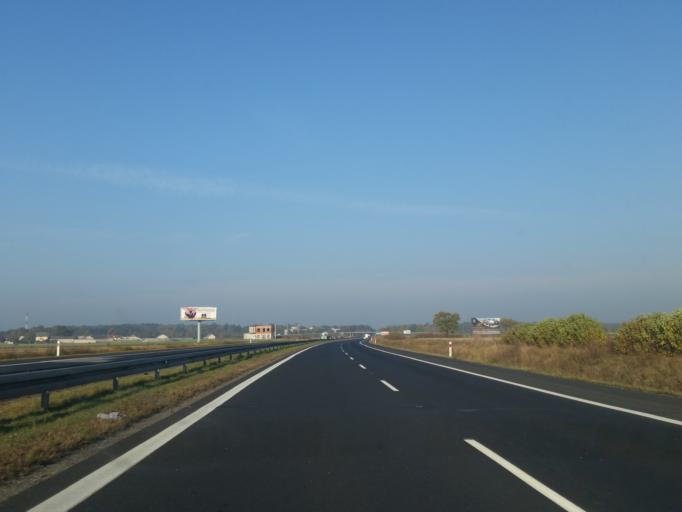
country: PL
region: Masovian Voivodeship
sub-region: Powiat nowodworski
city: Zakroczym
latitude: 52.4470
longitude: 20.6027
